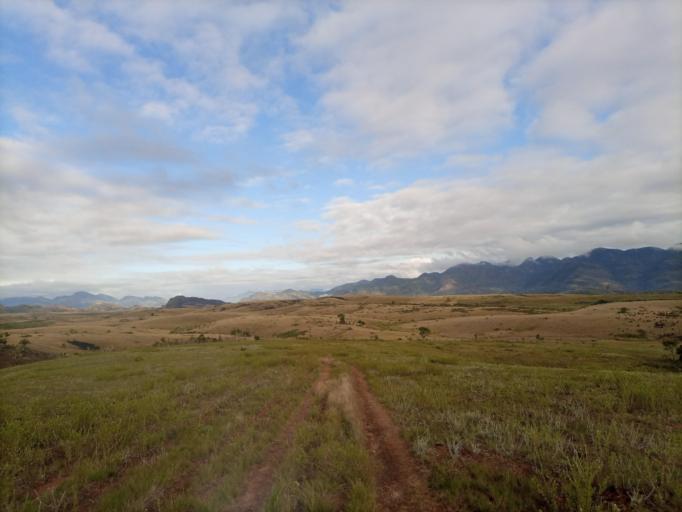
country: MG
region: Anosy
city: Fort Dauphin
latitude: -24.3087
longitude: 47.2474
